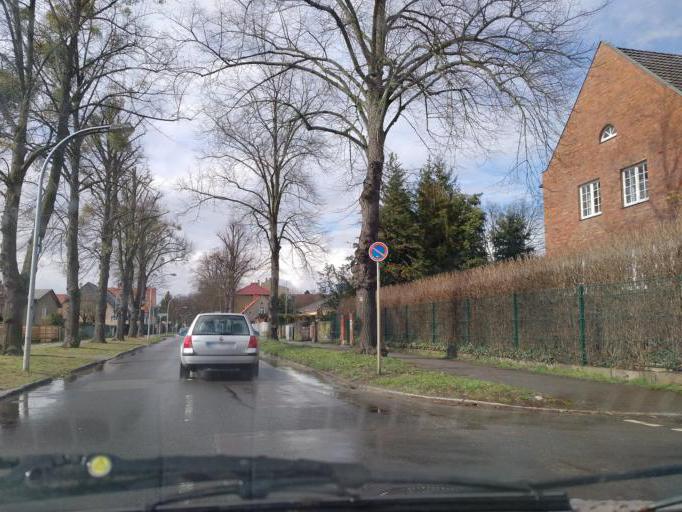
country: DE
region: Brandenburg
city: Falkensee
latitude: 52.5609
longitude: 13.0990
